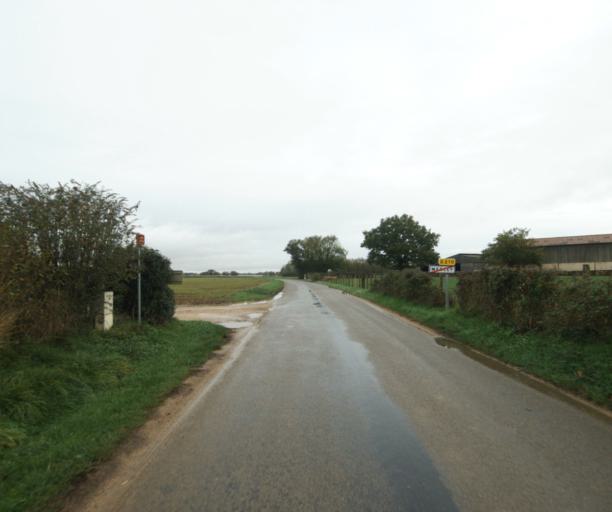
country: FR
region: Rhone-Alpes
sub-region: Departement de l'Ain
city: Pont-de-Vaux
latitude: 46.4857
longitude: 4.8687
